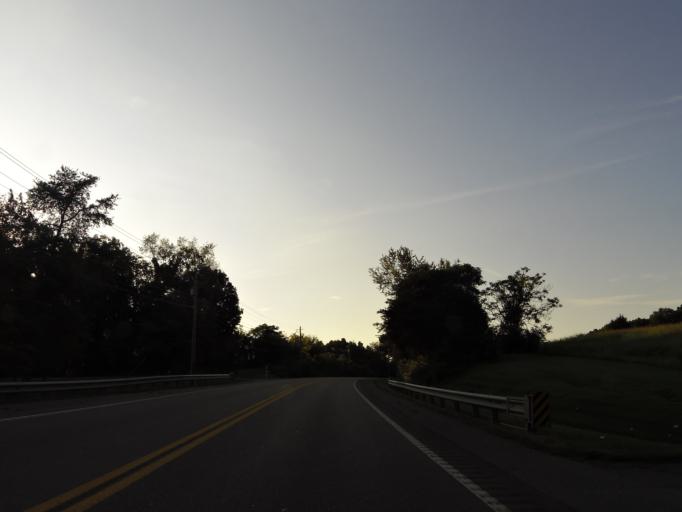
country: US
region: Tennessee
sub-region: McMinn County
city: Athens
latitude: 35.4869
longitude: -84.5983
